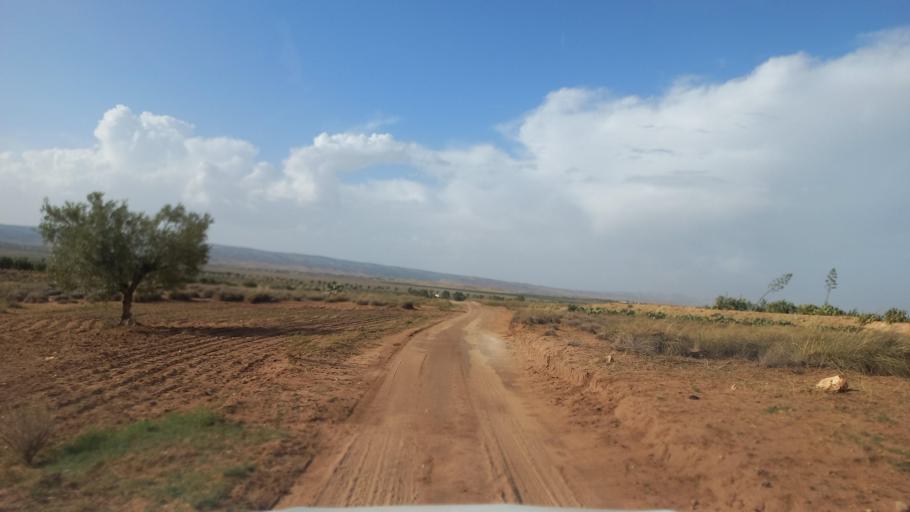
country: TN
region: Al Qasrayn
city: Kasserine
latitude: 35.2189
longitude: 8.9700
